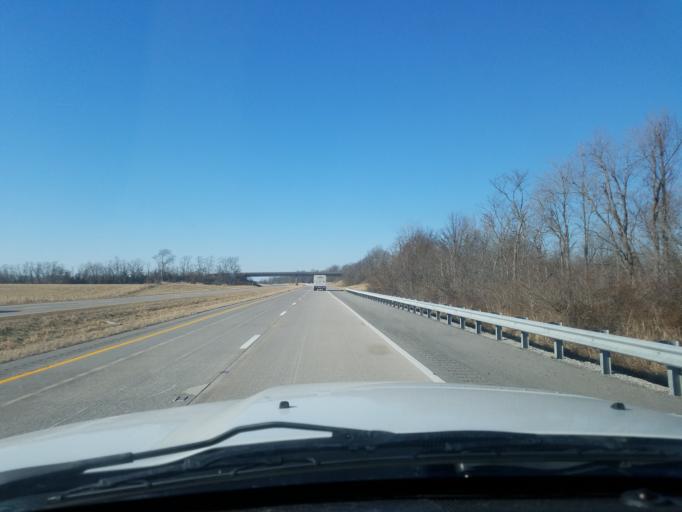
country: US
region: Kentucky
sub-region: Henderson County
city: Henderson
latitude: 37.7683
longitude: -87.4266
